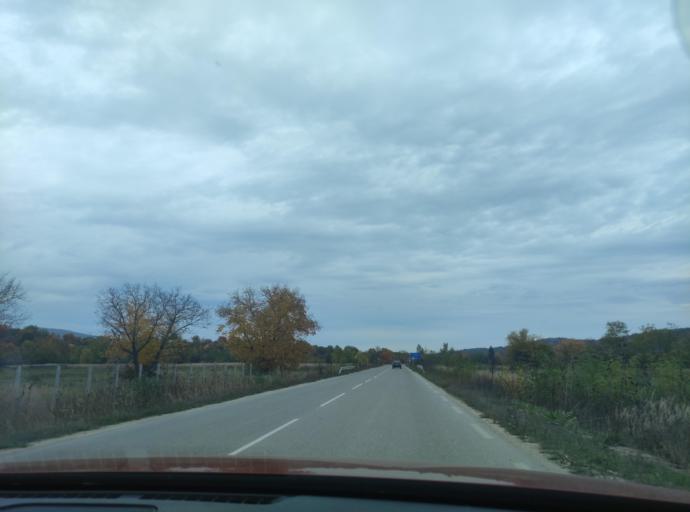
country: BG
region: Montana
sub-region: Obshtina Berkovitsa
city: Berkovitsa
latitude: 43.2494
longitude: 23.1679
